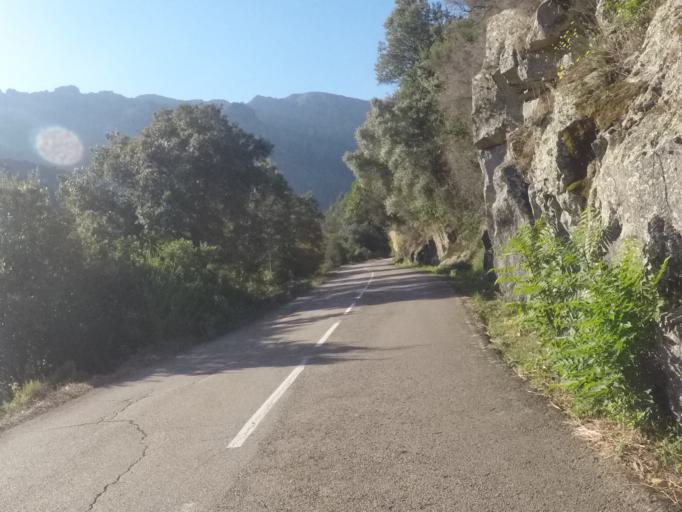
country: FR
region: Corsica
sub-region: Departement de la Corse-du-Sud
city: Cargese
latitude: 42.2466
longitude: 8.7303
